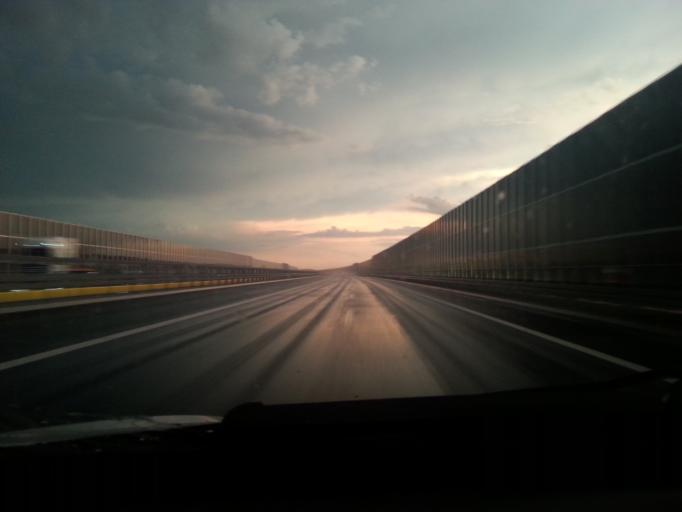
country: PL
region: Lodz Voivodeship
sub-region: Powiat pabianicki
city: Dobron
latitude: 51.5936
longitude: 19.2246
